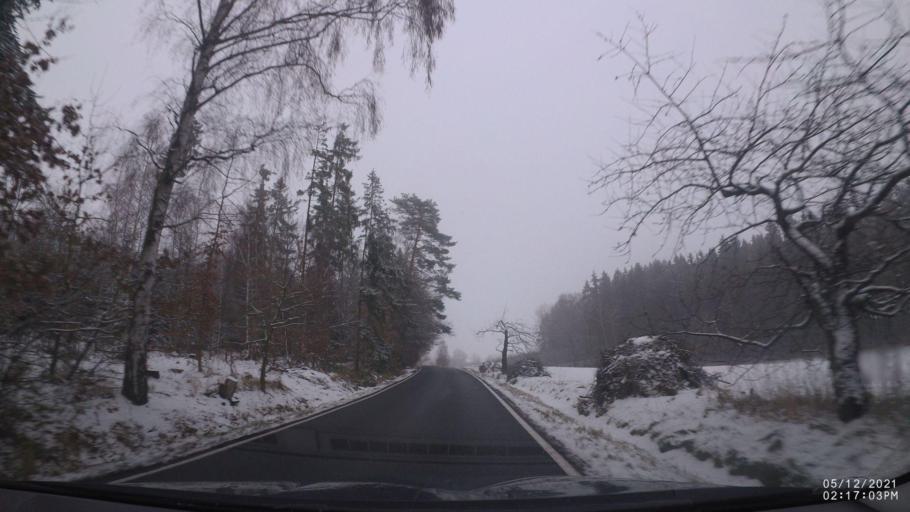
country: CZ
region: Kralovehradecky
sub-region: Okres Nachod
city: Cerveny Kostelec
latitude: 50.4672
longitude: 16.1229
